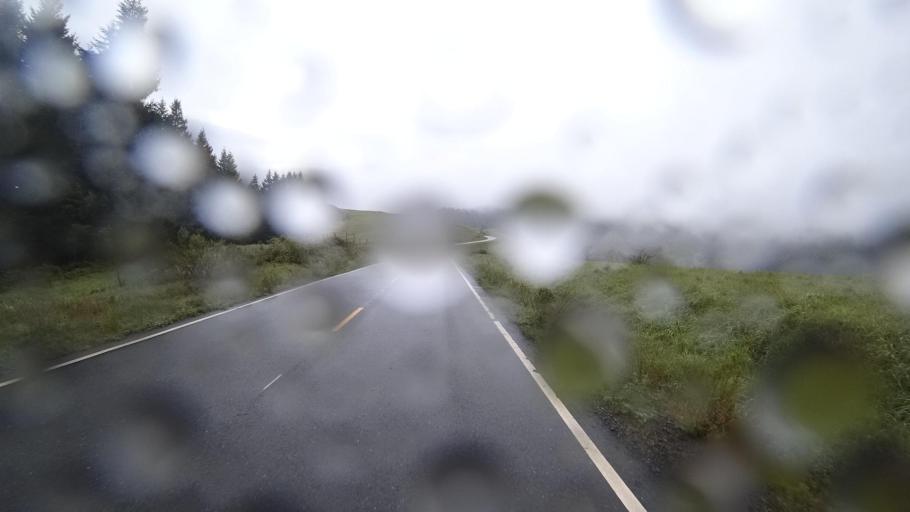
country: US
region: California
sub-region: Humboldt County
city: Westhaven-Moonstone
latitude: 41.1633
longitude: -123.9032
